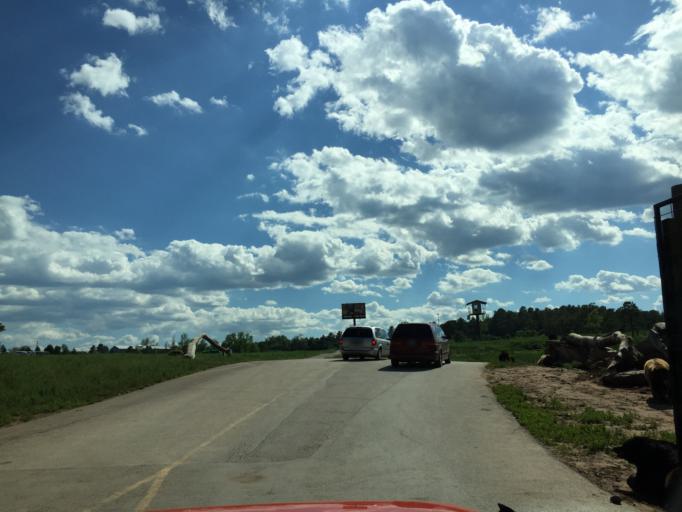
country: US
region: South Dakota
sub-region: Pennington County
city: Colonial Pine Hills
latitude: 43.9796
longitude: -103.2963
